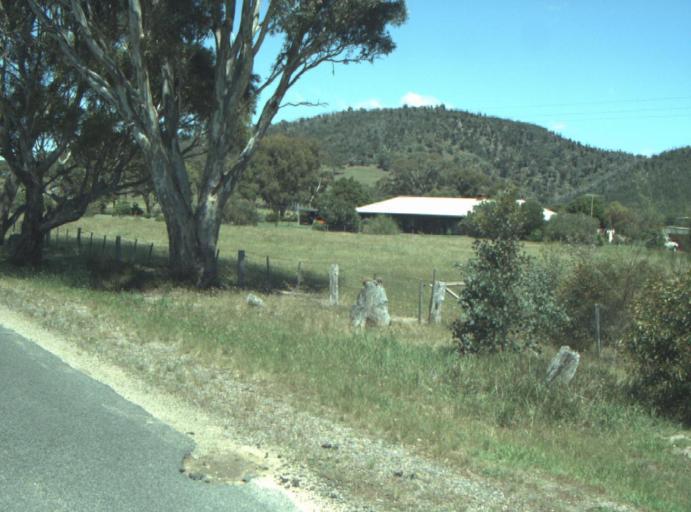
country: AU
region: Victoria
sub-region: Greater Geelong
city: Lara
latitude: -37.8571
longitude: 144.2806
